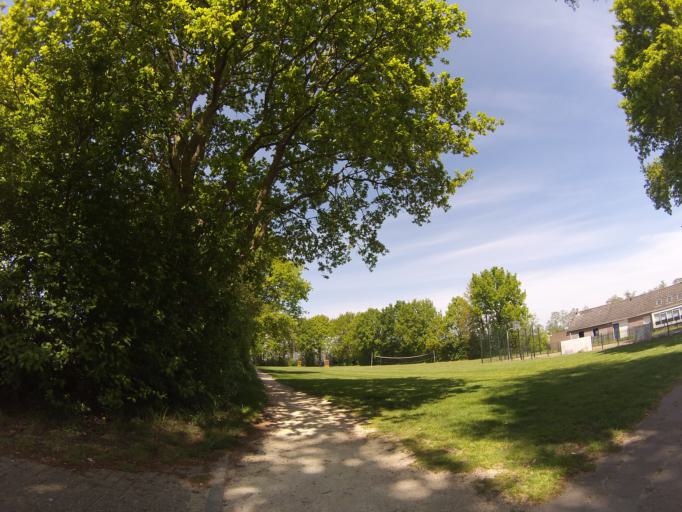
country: NL
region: Drenthe
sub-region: Gemeente Hoogeveen
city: Hoogeveen
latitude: 52.7486
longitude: 6.4976
